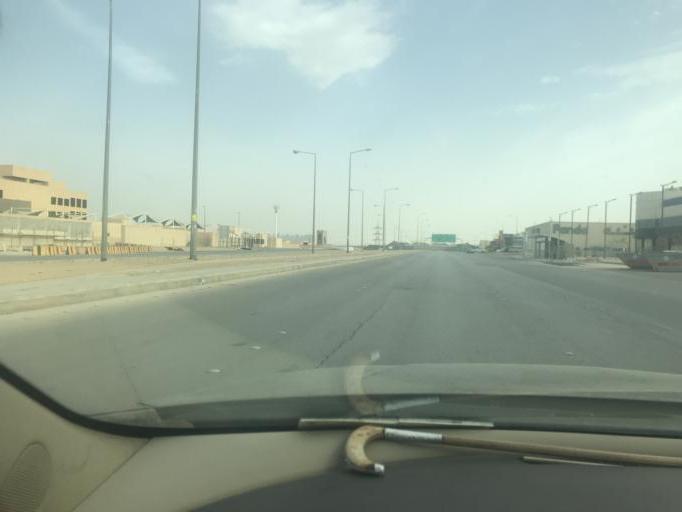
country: SA
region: Ar Riyad
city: Riyadh
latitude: 24.8087
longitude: 46.6923
